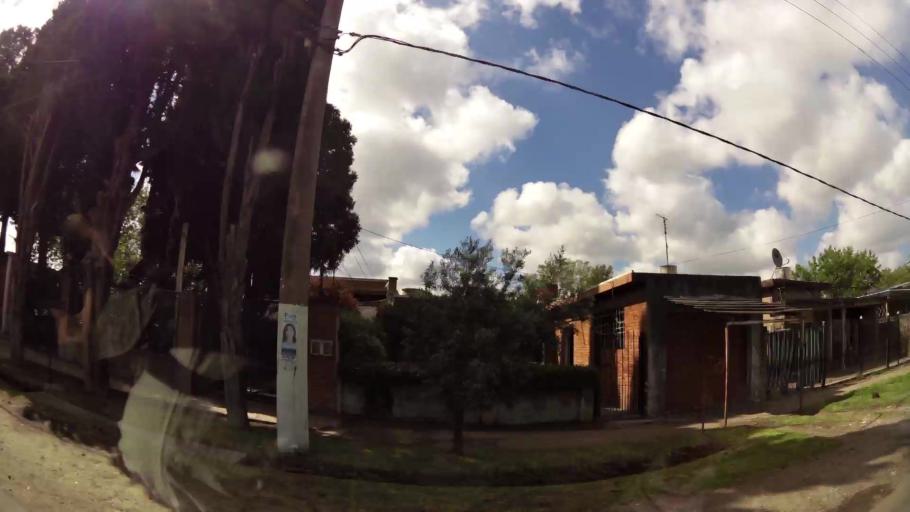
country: AR
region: Buenos Aires
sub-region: Partido de Quilmes
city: Quilmes
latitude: -34.8297
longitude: -58.1740
